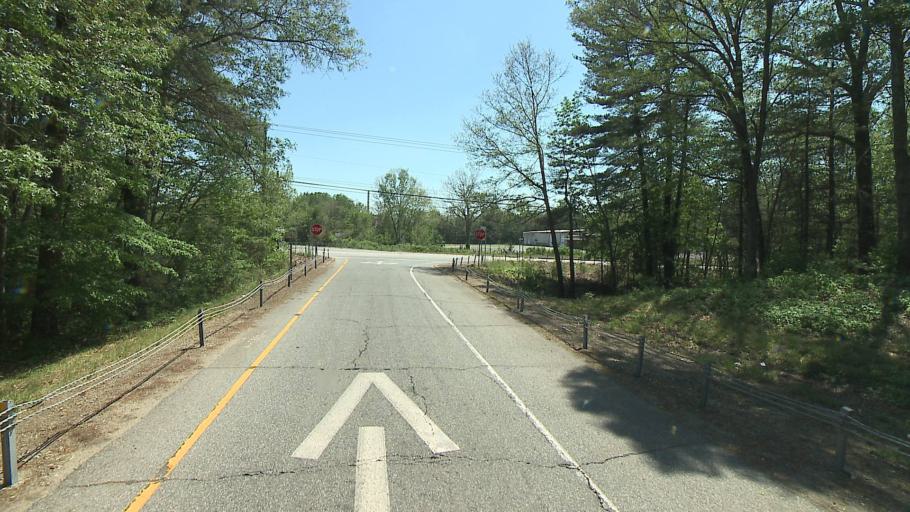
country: US
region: Connecticut
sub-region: Windham County
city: Killingly Center
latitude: 41.8678
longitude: -71.8911
